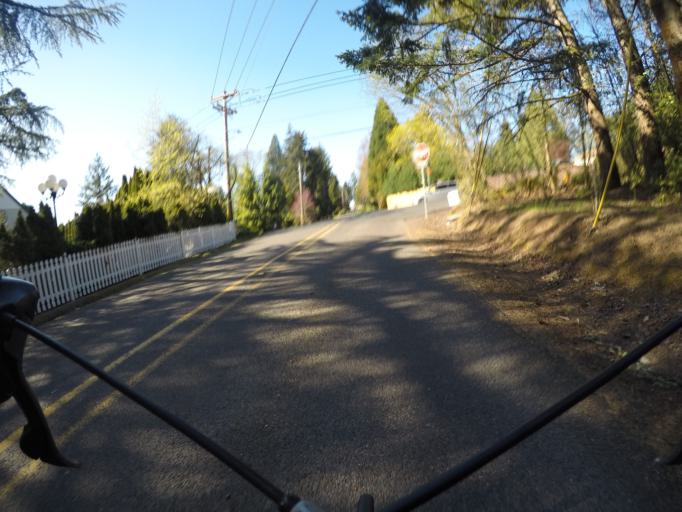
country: US
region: Oregon
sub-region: Washington County
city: King City
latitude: 45.4151
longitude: -122.8314
